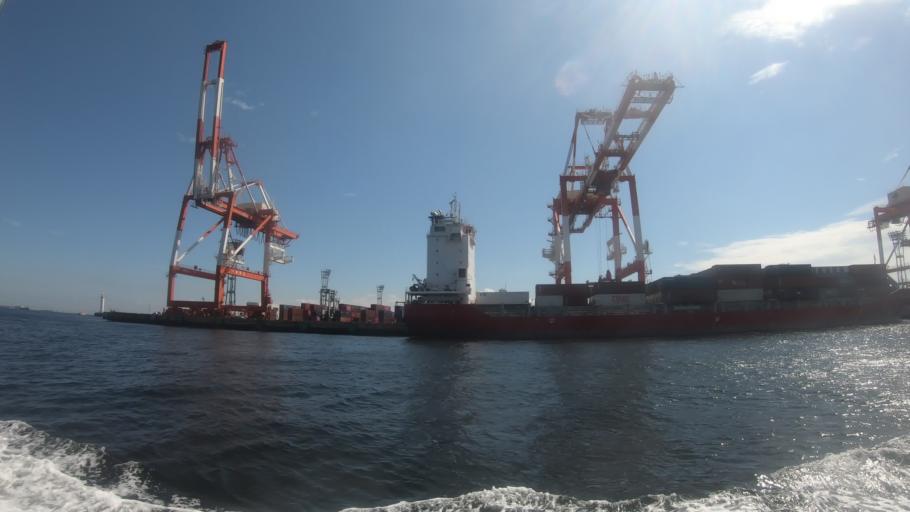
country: JP
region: Kanagawa
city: Yokohama
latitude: 35.4413
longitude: 139.6834
